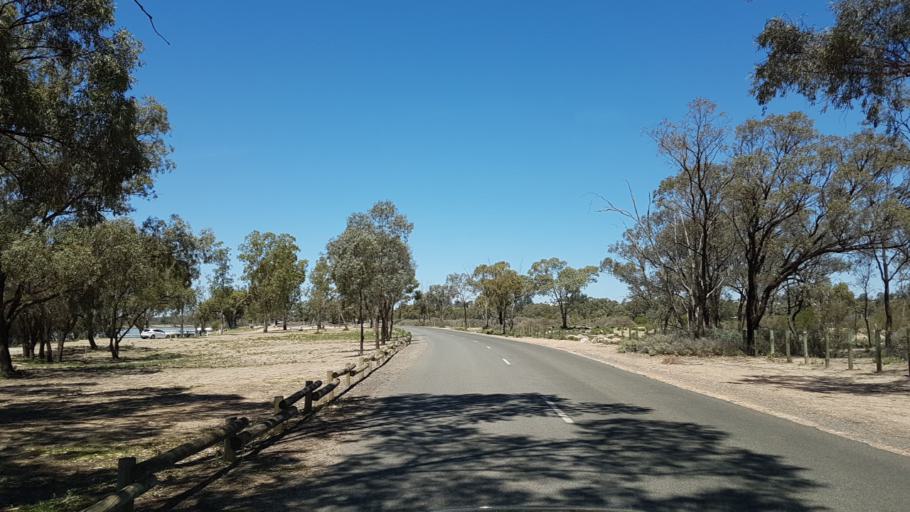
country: AU
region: South Australia
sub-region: Loxton Waikerie
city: Waikerie
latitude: -34.1693
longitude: 139.9758
